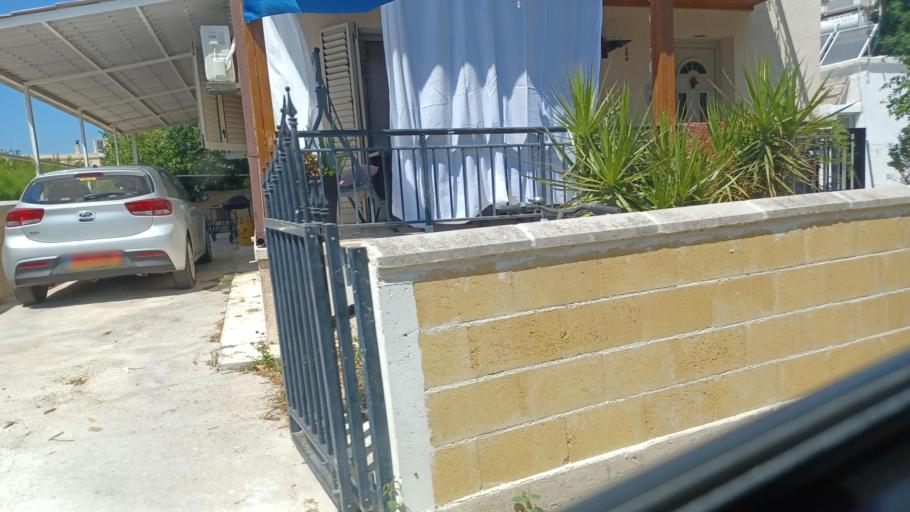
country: CY
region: Pafos
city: Paphos
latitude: 34.7381
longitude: 32.4850
